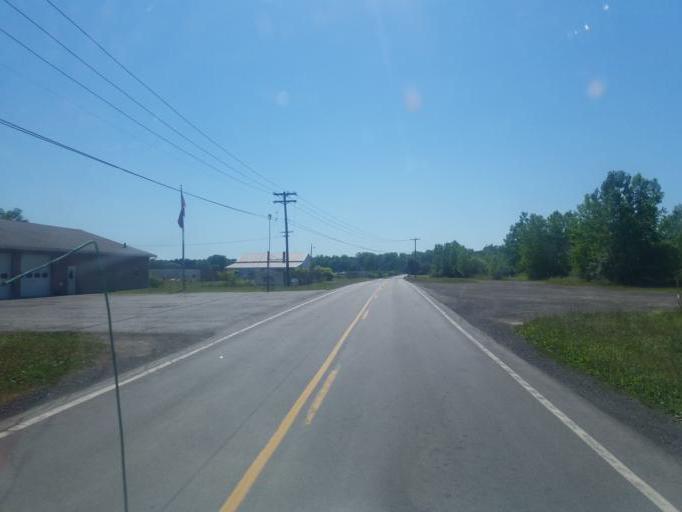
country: US
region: New York
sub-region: Ontario County
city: Phelps
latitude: 42.9330
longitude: -77.0003
